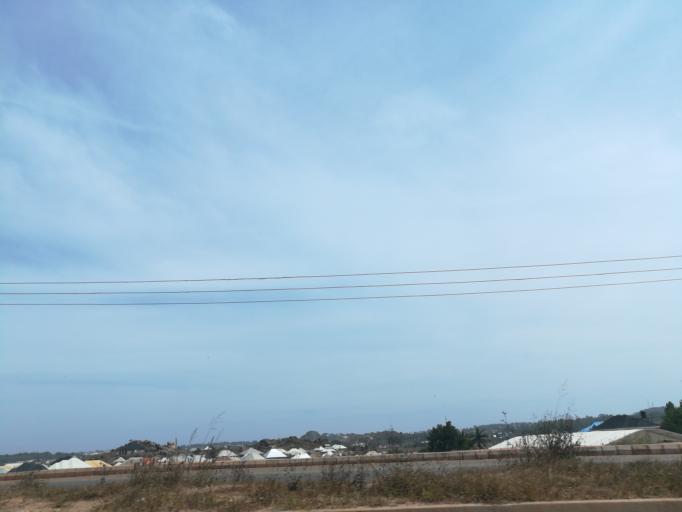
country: NG
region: Plateau
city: Bukuru
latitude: 9.8259
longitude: 8.8661
